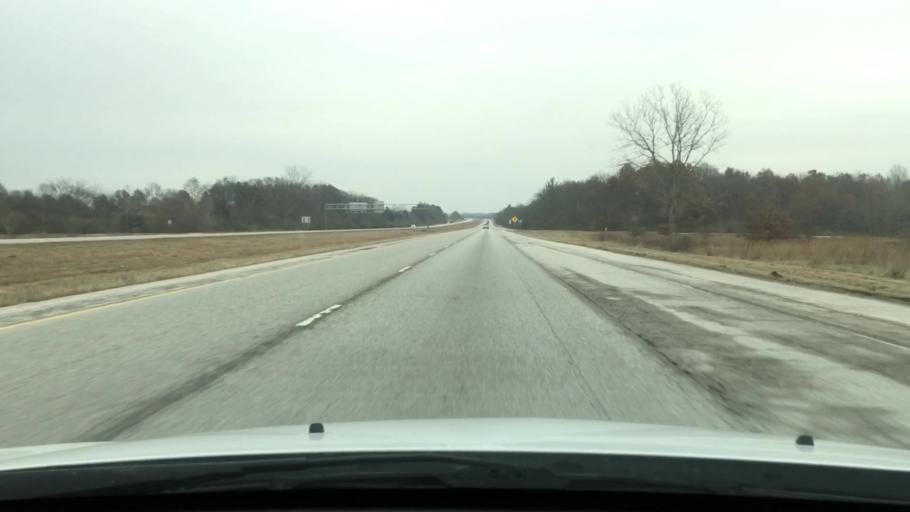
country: US
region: Illinois
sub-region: Morgan County
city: South Jacksonville
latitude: 39.6802
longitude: -90.2925
